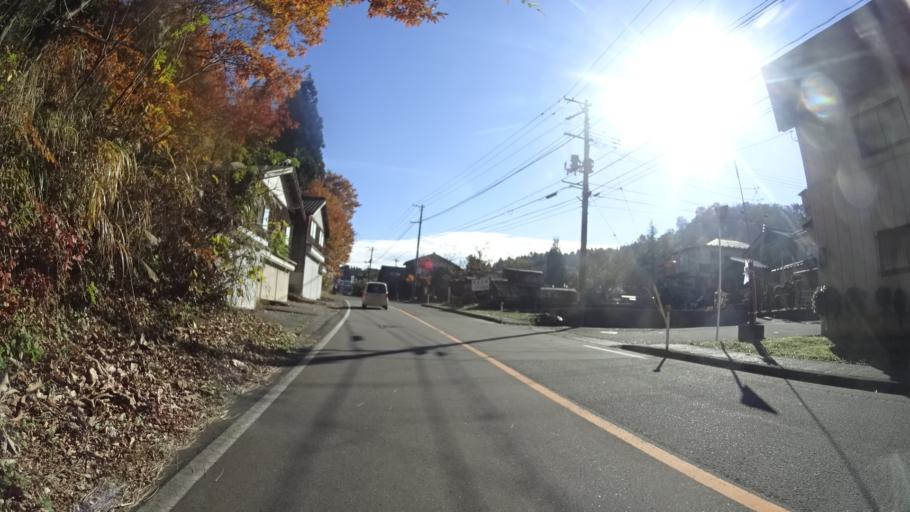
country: JP
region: Niigata
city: Tochio-honcho
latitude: 37.4835
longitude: 138.9820
